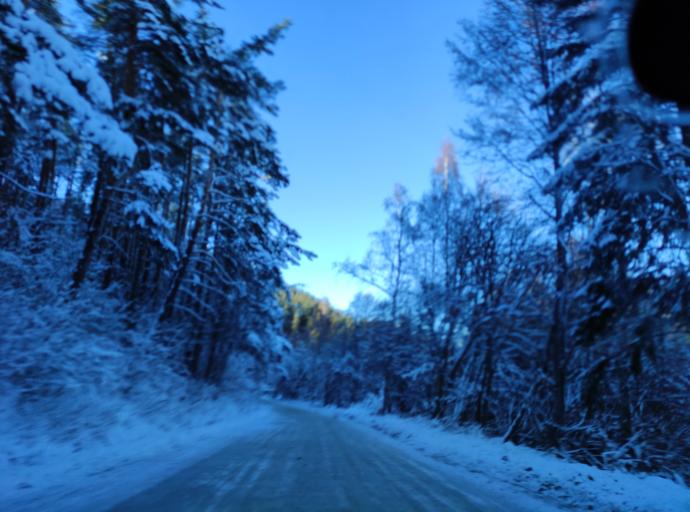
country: BG
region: Sofia-Capital
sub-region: Stolichna Obshtina
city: Sofia
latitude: 42.5985
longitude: 23.3050
